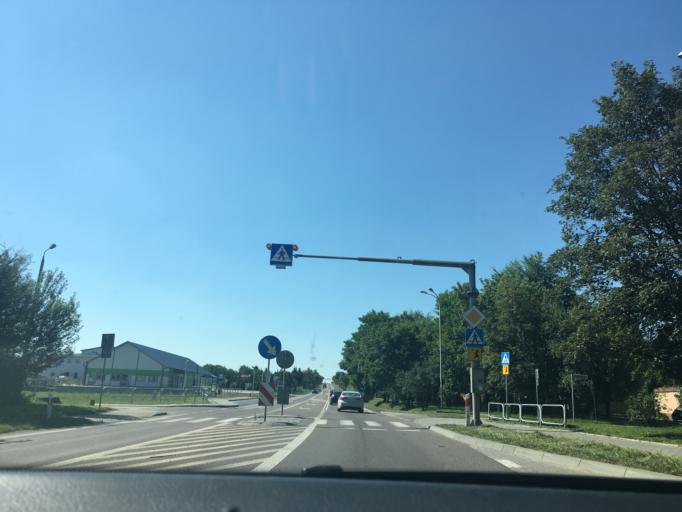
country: PL
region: Lublin Voivodeship
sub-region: Powiat lubelski
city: Niemce
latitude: 51.3569
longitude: 22.6212
